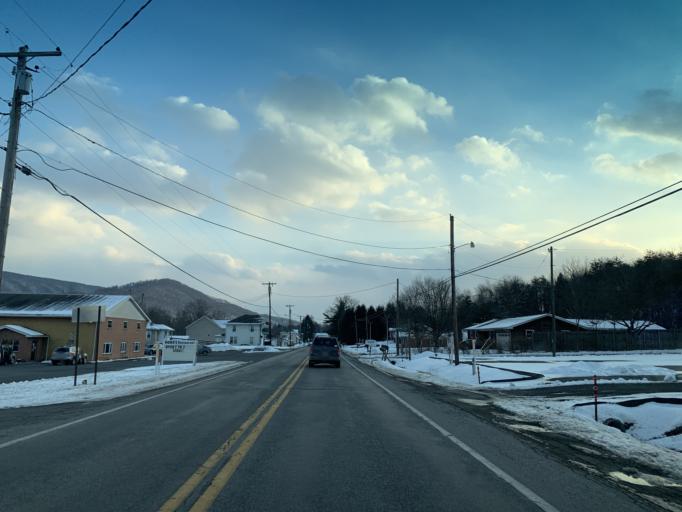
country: US
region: Maryland
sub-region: Allegany County
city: Cumberland
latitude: 39.7264
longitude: -78.7734
